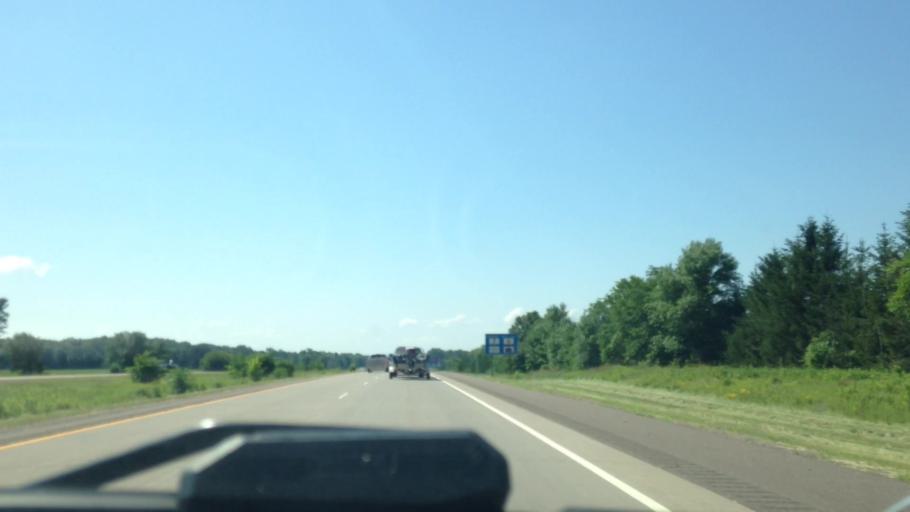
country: US
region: Wisconsin
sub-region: Barron County
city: Rice Lake
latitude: 45.4859
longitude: -91.7621
